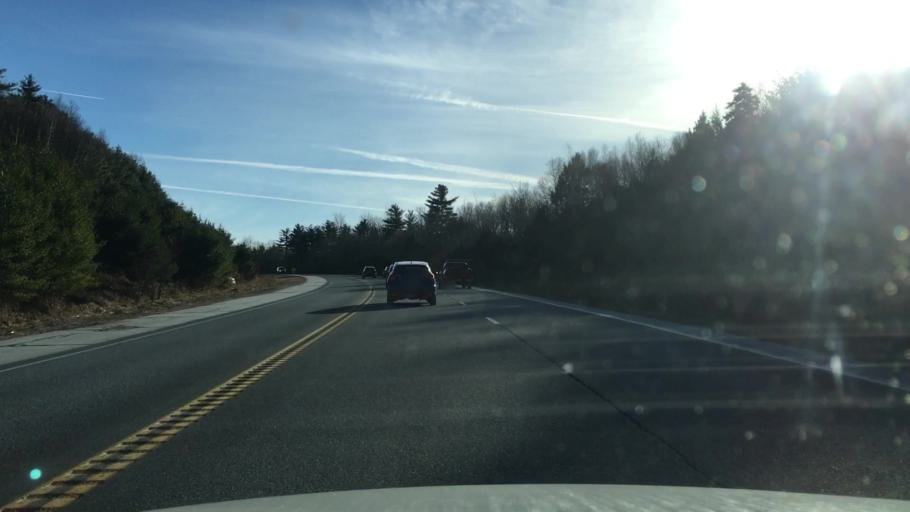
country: US
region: Maine
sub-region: Hancock County
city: Dedham
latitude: 44.6752
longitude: -68.5787
